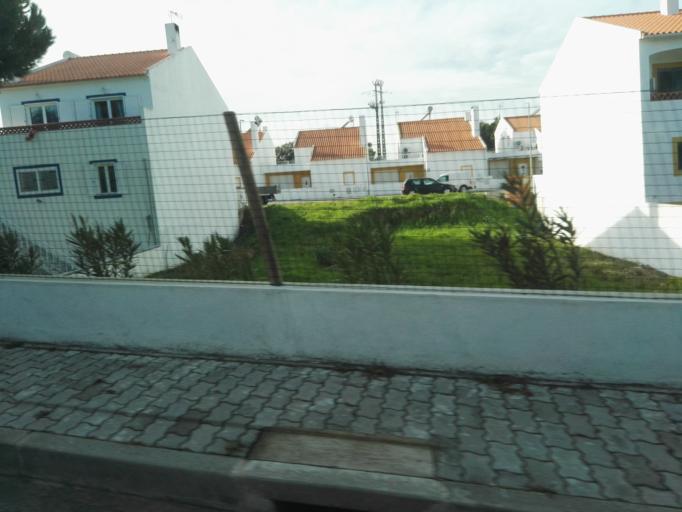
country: PT
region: Evora
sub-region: Mora
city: Mora
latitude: 38.9379
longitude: -8.1660
